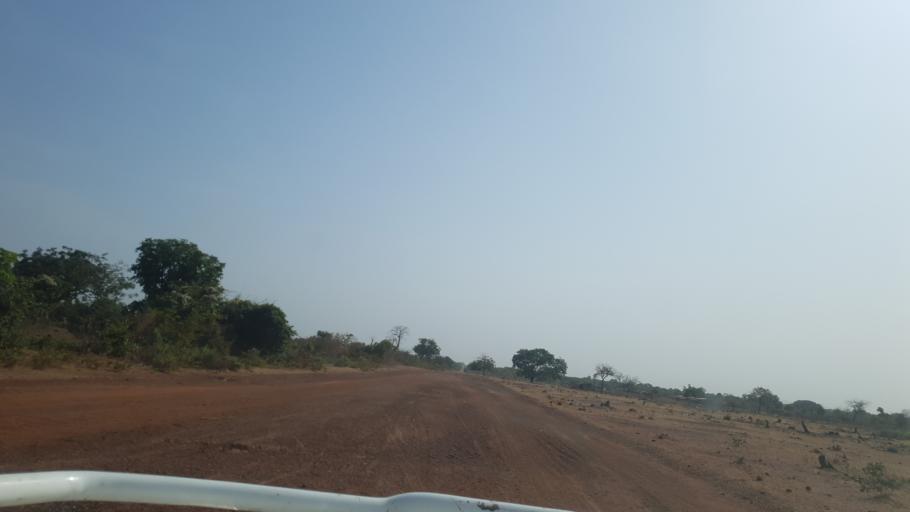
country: ML
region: Koulikoro
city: Dioila
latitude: 12.6679
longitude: -6.6921
